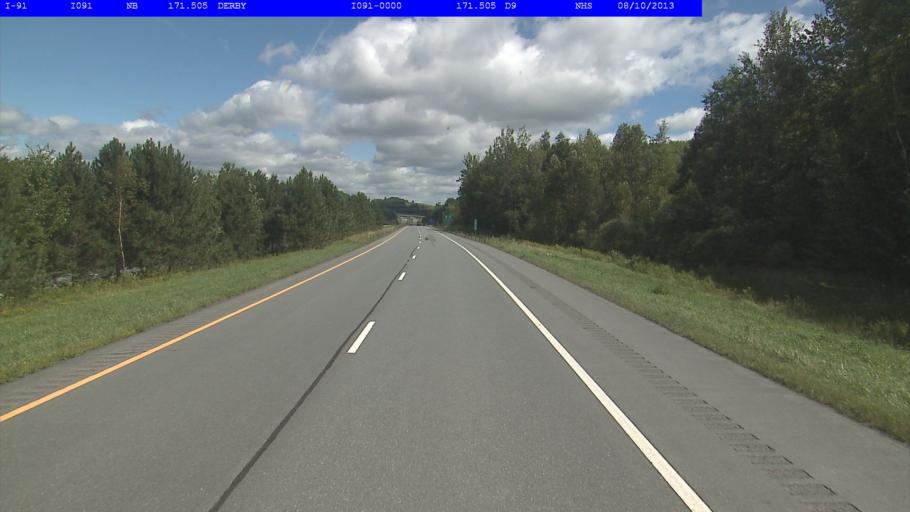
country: US
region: Vermont
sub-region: Orleans County
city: Newport
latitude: 44.9409
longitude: -72.1591
